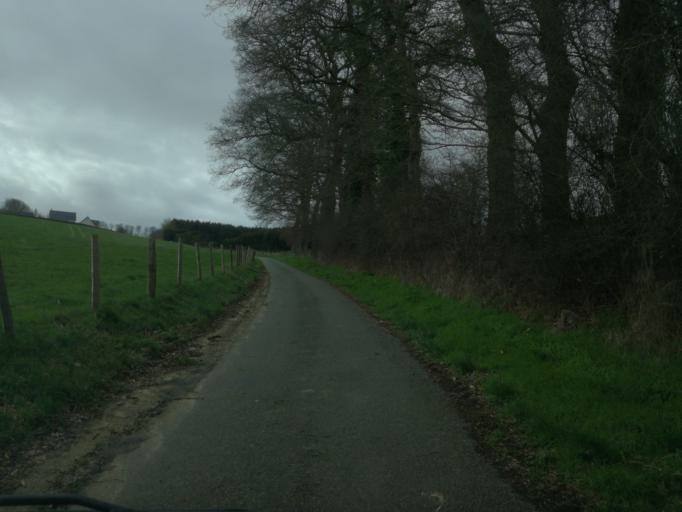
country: FR
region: Haute-Normandie
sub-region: Departement de la Seine-Maritime
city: Yebleron
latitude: 49.6789
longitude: 0.4941
